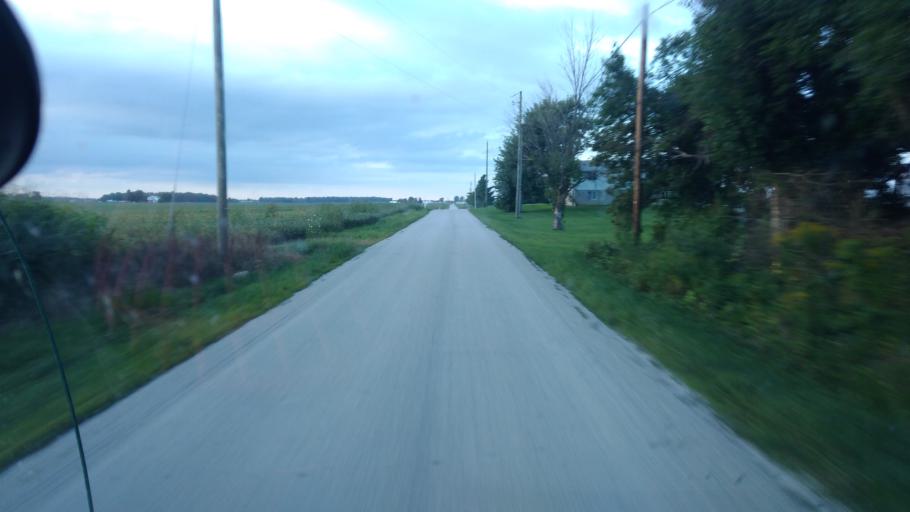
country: US
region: Ohio
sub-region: Hardin County
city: Kenton
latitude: 40.6648
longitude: -83.5147
